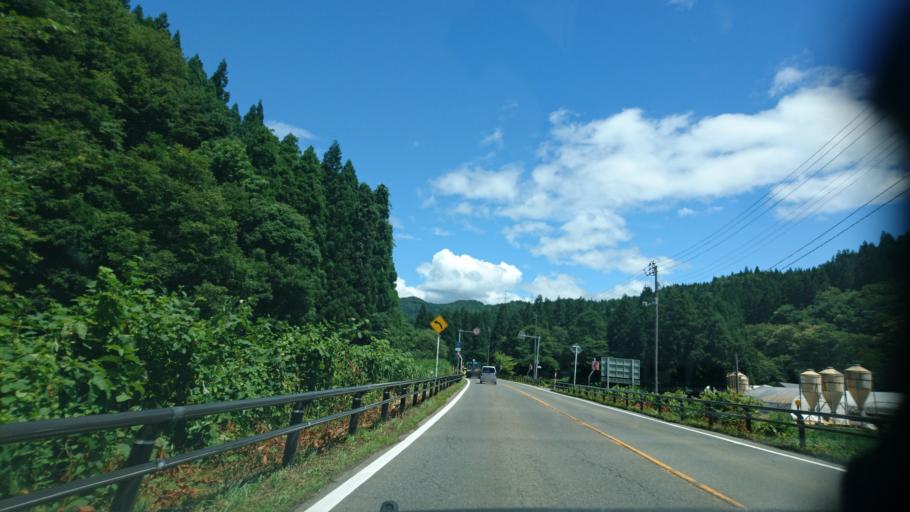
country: JP
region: Akita
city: Kakunodatemachi
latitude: 39.6539
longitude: 140.6719
